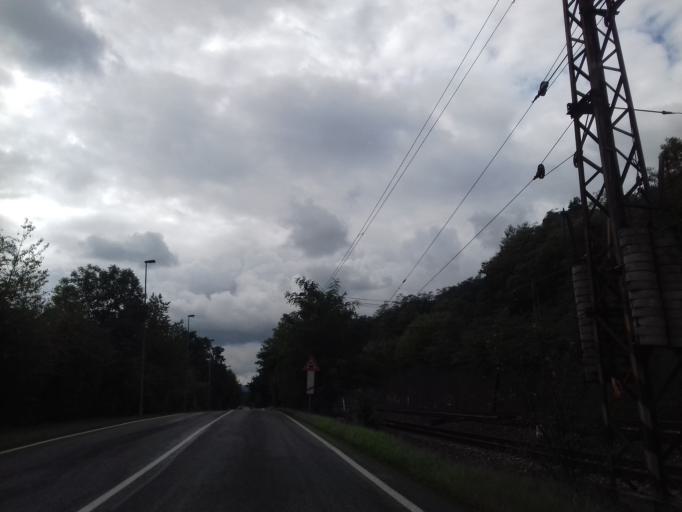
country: CZ
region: Praha
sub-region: Praha 12
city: Modrany
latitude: 49.9933
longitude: 14.3742
